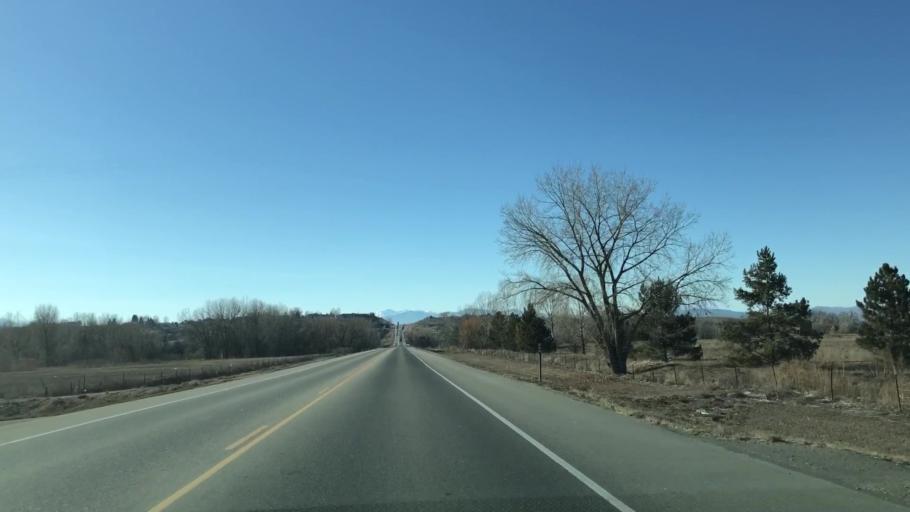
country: US
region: Colorado
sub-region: Weld County
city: Windsor
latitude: 40.4793
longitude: -104.9488
